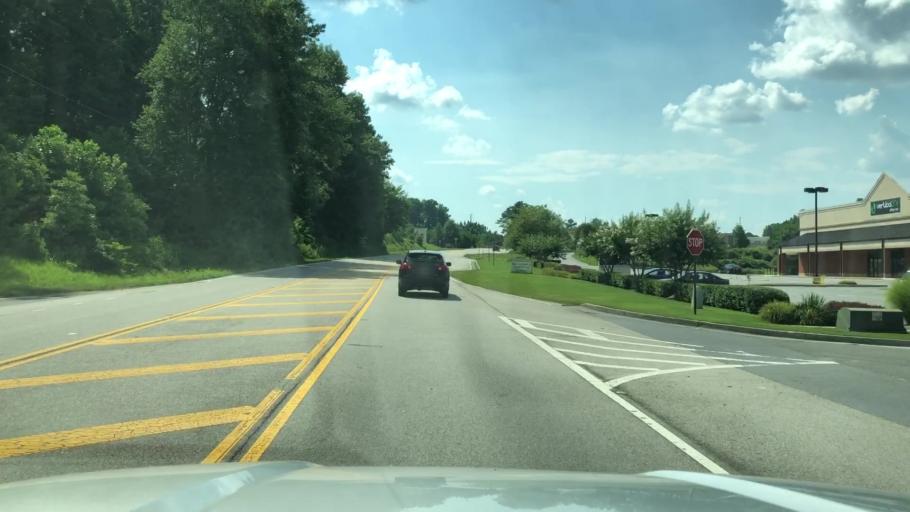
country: US
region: Georgia
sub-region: Paulding County
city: Dallas
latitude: 33.9556
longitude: -84.7843
